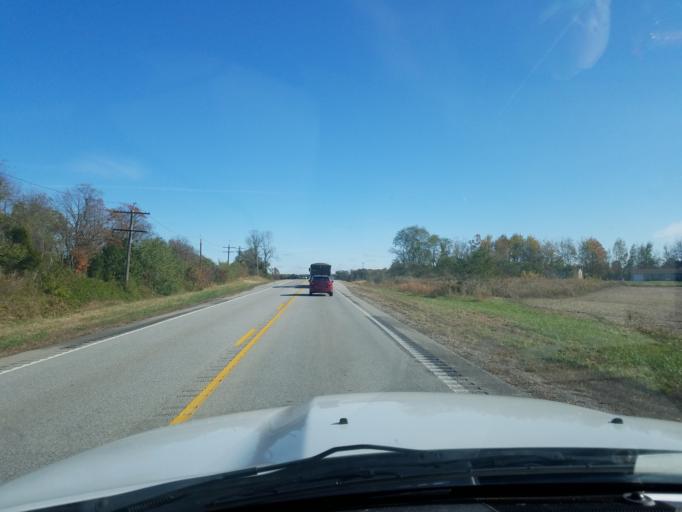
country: US
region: Indiana
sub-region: Jennings County
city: Country Squire Lakes
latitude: 38.9836
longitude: -85.6872
